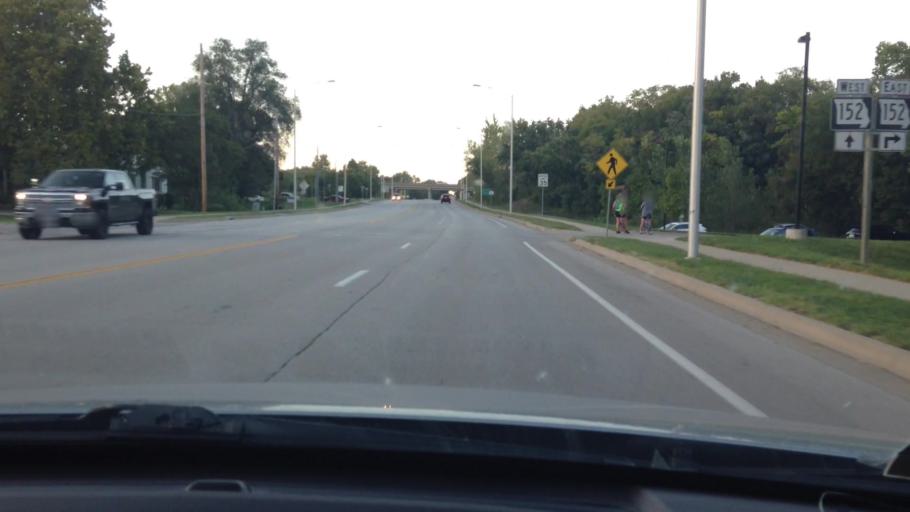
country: US
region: Missouri
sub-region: Platte County
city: Weatherby Lake
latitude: 39.2502
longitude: -94.6870
